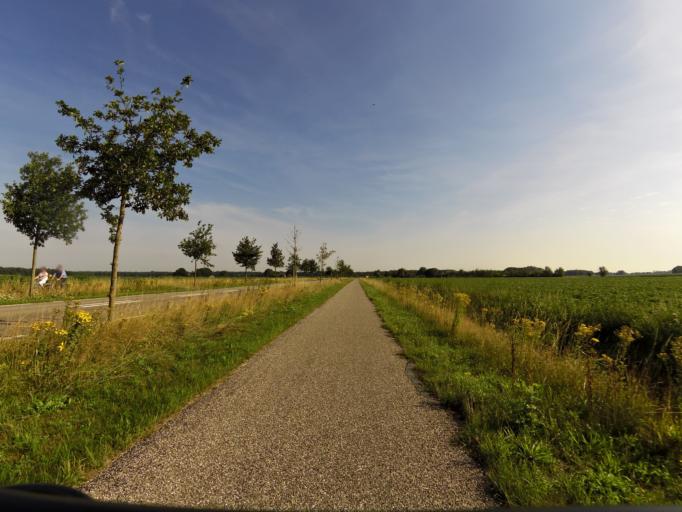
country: NL
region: North Brabant
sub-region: Gemeente Woensdrecht
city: Woensdrecht
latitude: 51.4431
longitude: 4.3783
